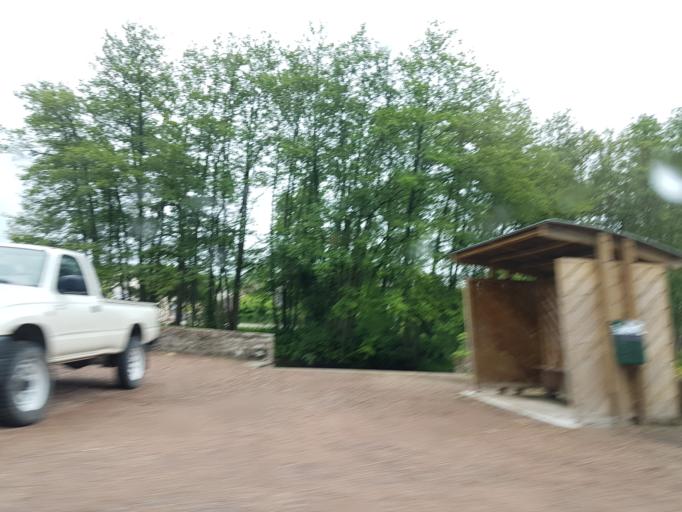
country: FR
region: Bourgogne
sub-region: Departement de la Nievre
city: Lormes
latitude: 47.1776
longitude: 3.7878
